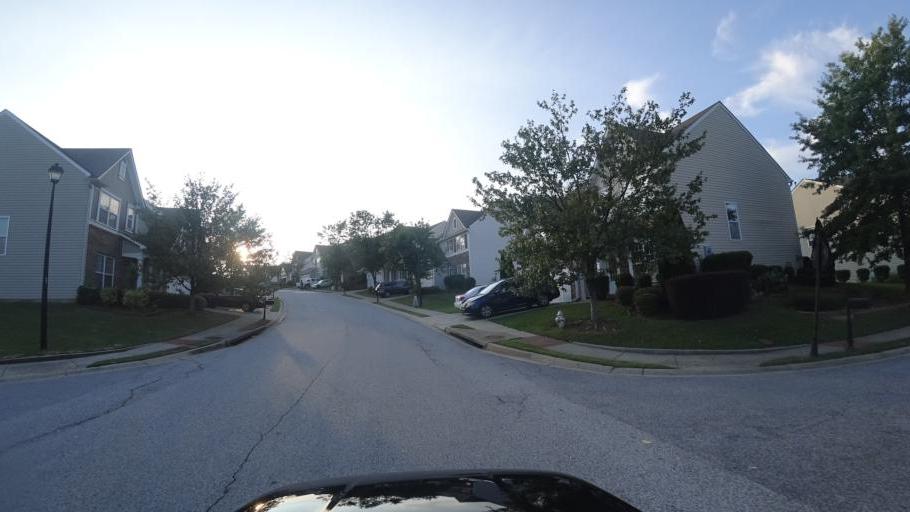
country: US
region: Georgia
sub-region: Gwinnett County
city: Duluth
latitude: 33.9563
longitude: -84.1142
